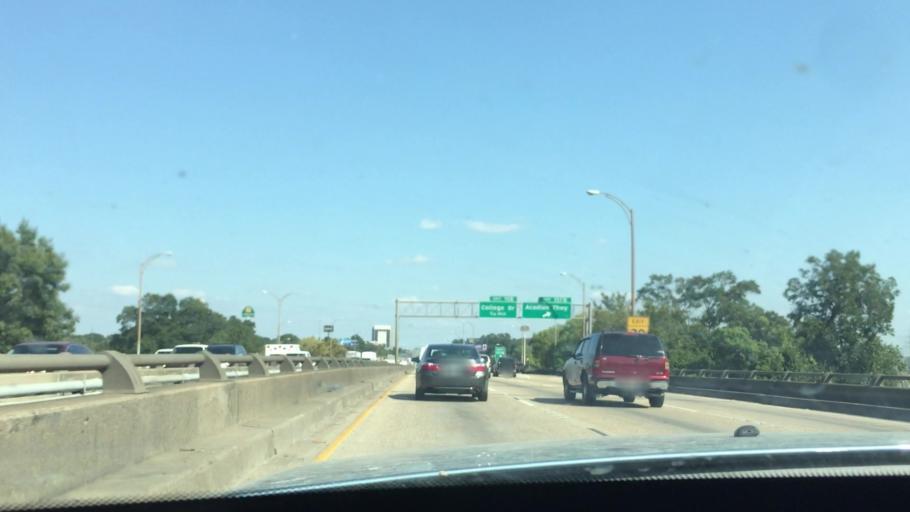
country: US
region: Louisiana
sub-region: East Baton Rouge Parish
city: Baton Rouge
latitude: 30.4246
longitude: -91.1551
